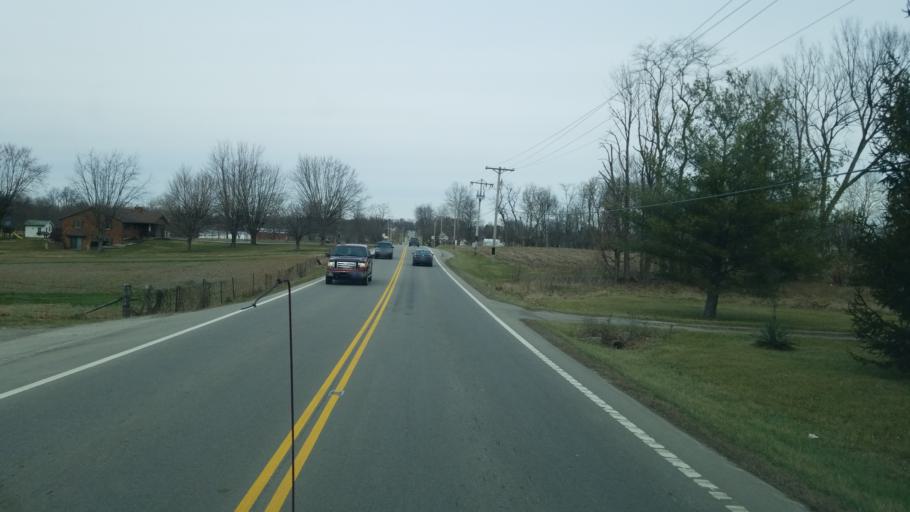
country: US
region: Ohio
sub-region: Highland County
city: Hillsboro
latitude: 39.1377
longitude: -83.6679
